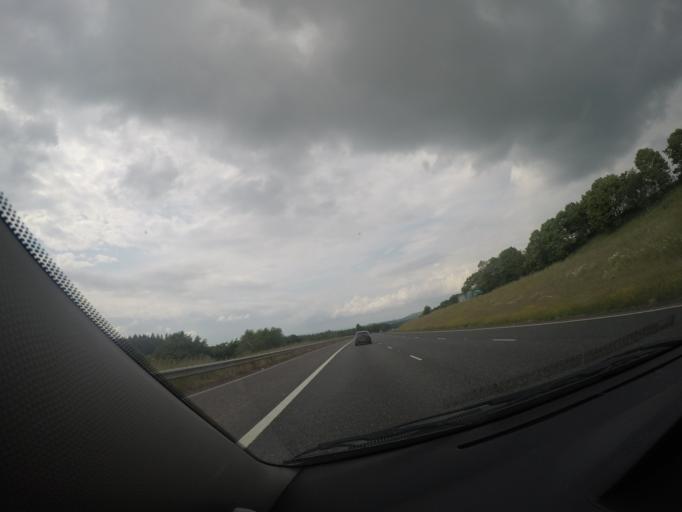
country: GB
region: Scotland
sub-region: Dumfries and Galloway
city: Lockerbie
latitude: 55.0810
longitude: -3.3152
